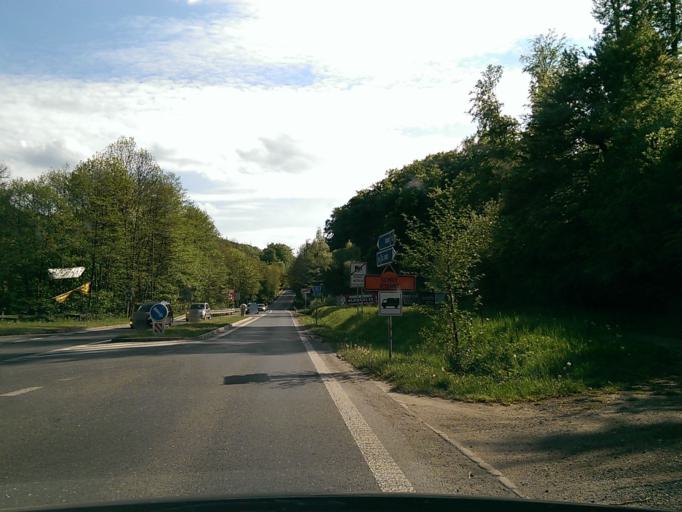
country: CZ
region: Liberecky
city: Mala Skala
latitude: 50.6371
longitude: 15.1891
